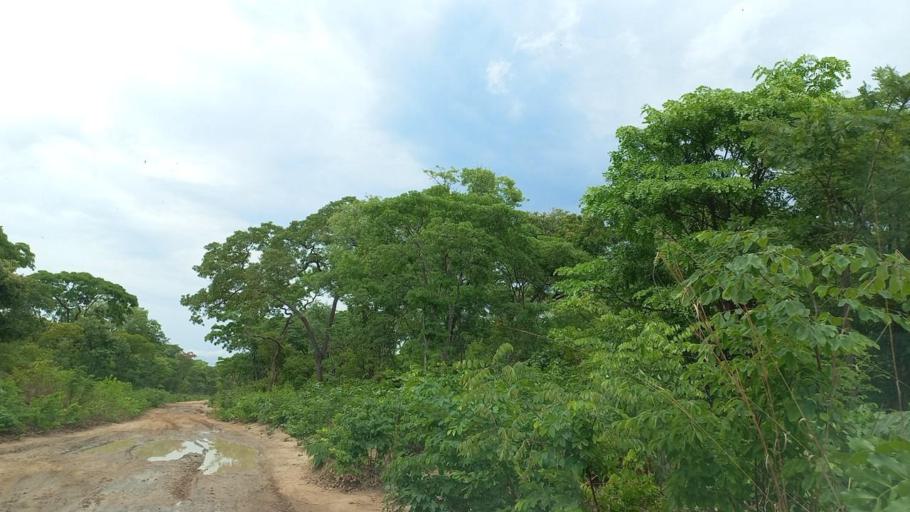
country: ZM
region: North-Western
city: Kalengwa
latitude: -13.5513
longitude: 24.9754
